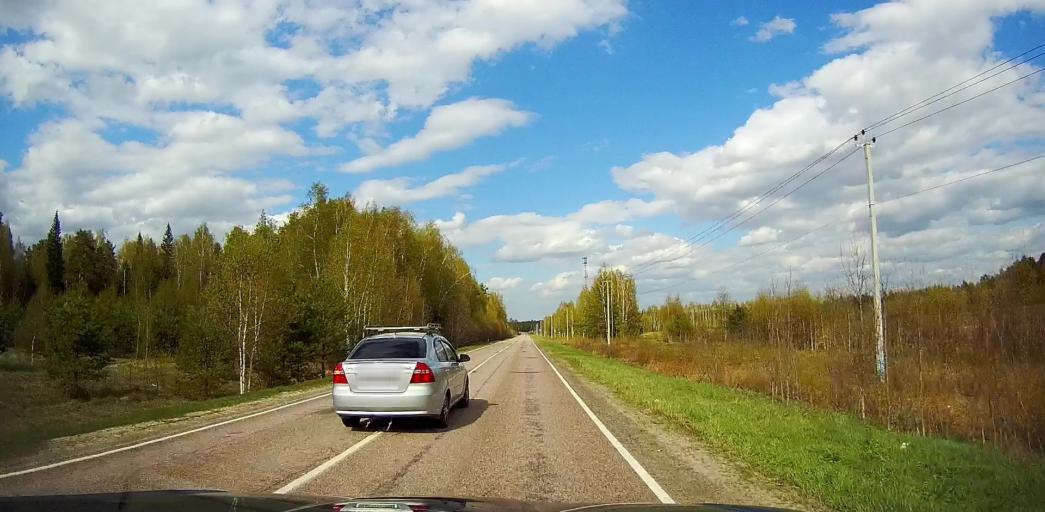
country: RU
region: Moskovskaya
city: Rakhmanovo
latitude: 55.6645
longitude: 38.6414
